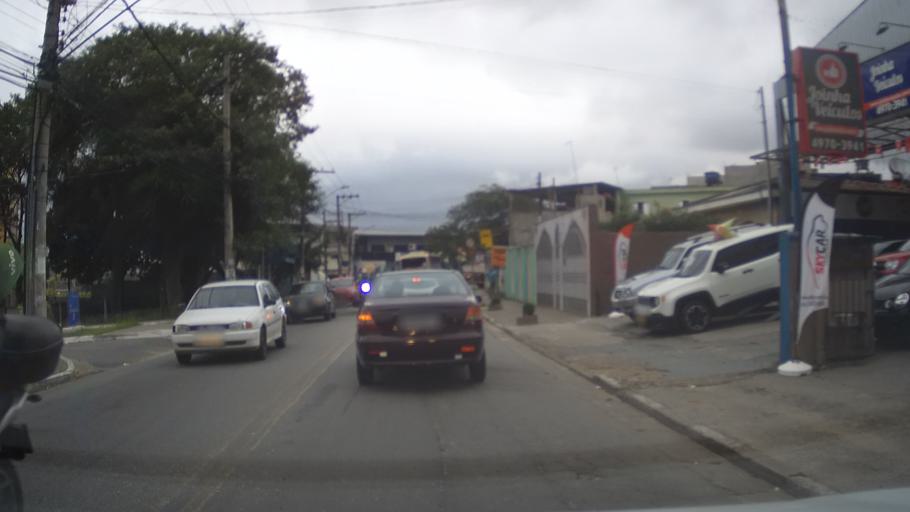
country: BR
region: Sao Paulo
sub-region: Guarulhos
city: Guarulhos
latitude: -23.4132
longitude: -46.4487
